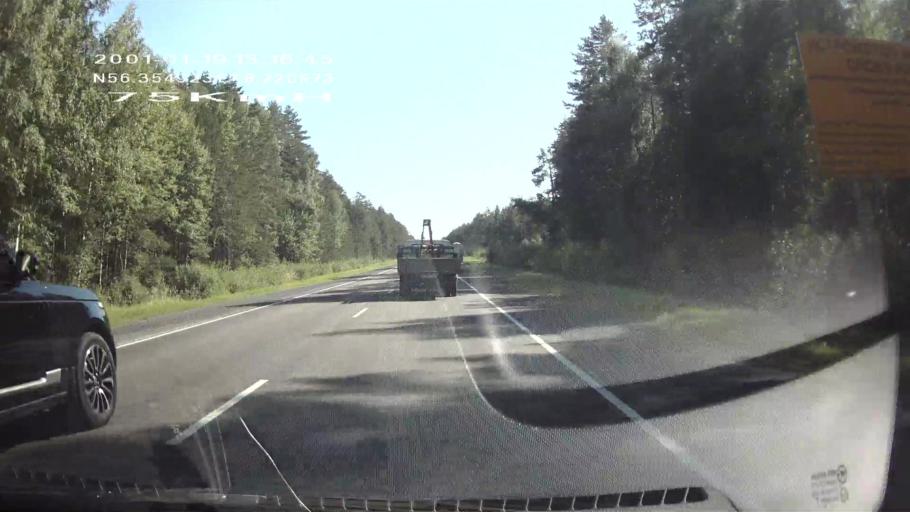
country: RU
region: Mariy-El
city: Suslonger
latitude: 56.3546
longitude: 48.2212
